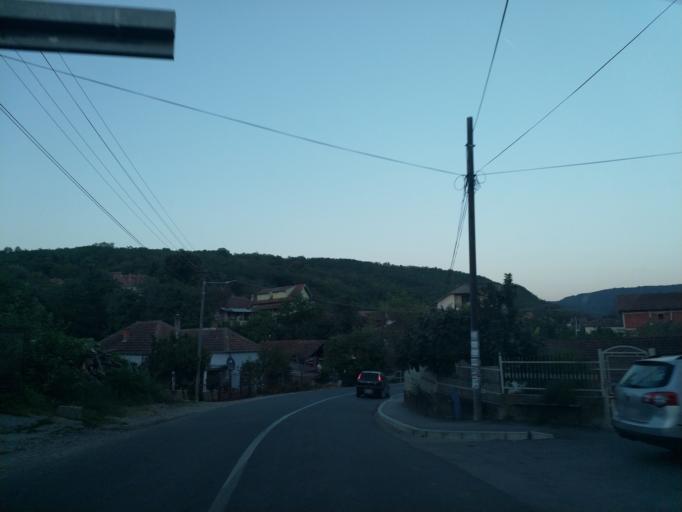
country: RS
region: Central Serbia
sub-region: Rasinski Okrug
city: Krusevac
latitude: 43.6247
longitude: 21.3554
